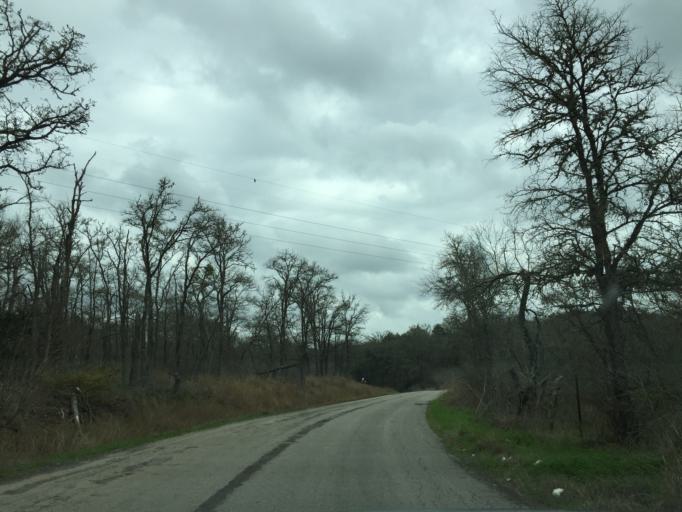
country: US
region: Texas
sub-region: Bastrop County
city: Bastrop
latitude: 30.1228
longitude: -97.3058
